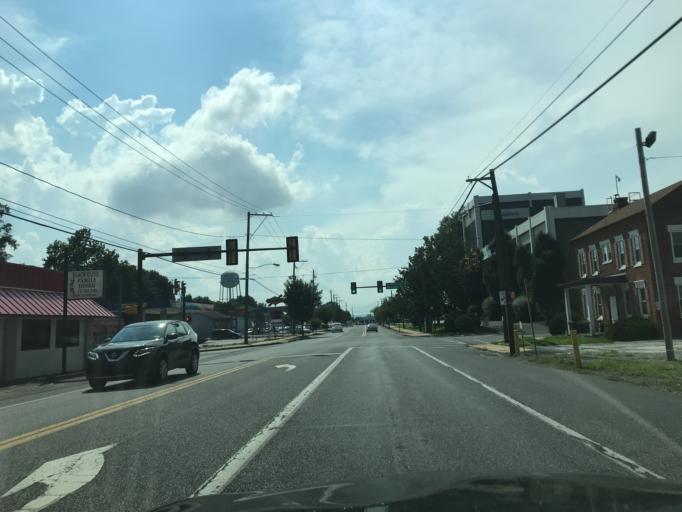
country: US
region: Pennsylvania
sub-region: Lancaster County
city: Columbia
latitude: 40.0315
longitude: -76.4808
